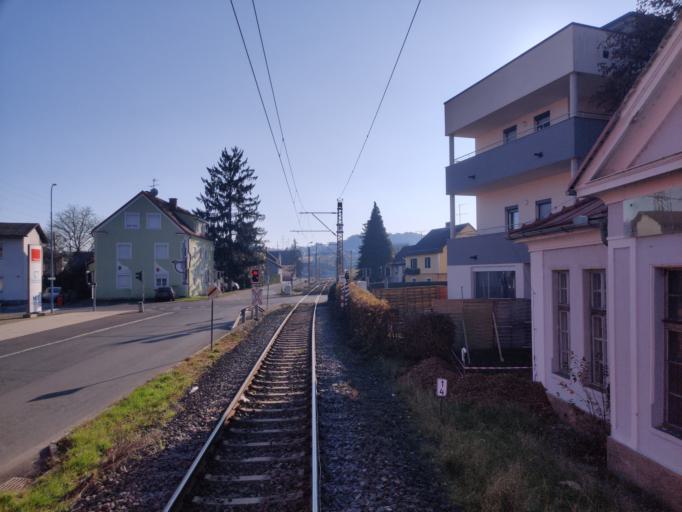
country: AT
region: Styria
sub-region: Politischer Bezirk Suedoststeiermark
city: Feldbach
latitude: 46.9516
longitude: 15.8978
